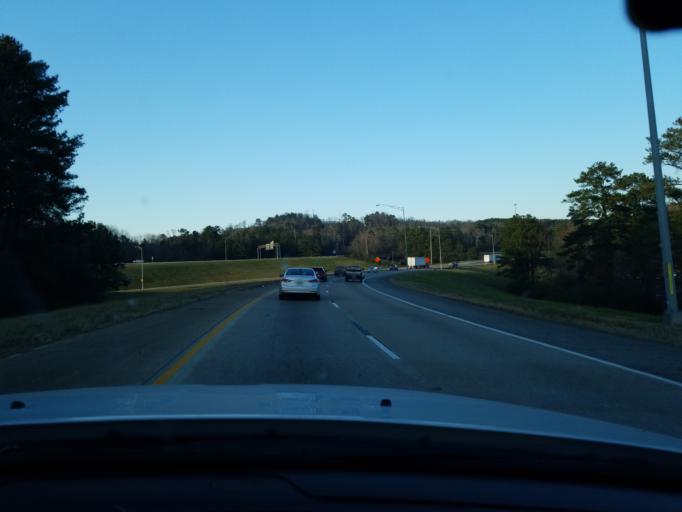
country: US
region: Alabama
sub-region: Jefferson County
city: Trussville
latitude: 33.5977
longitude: -86.6519
